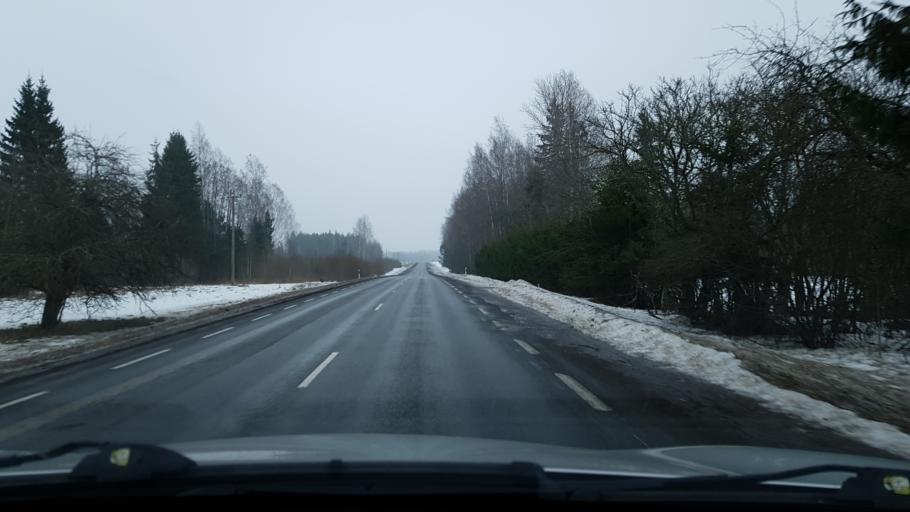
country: EE
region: Viljandimaa
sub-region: Viiratsi vald
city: Viiratsi
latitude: 58.2500
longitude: 25.7607
